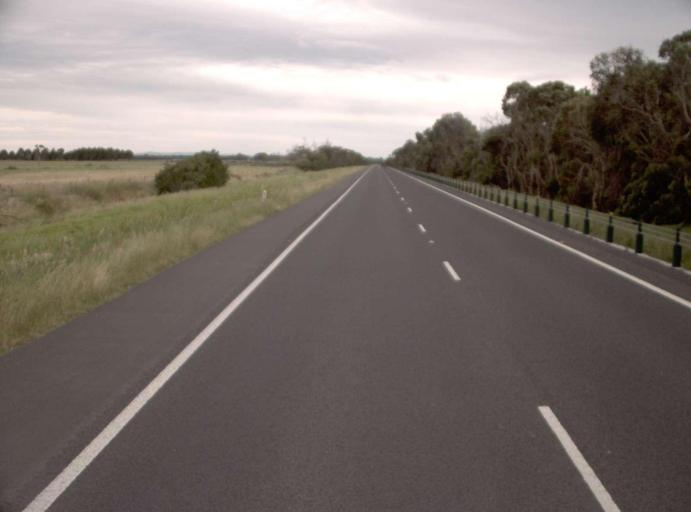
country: AU
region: Victoria
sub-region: Casey
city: Junction Village
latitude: -38.1679
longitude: 145.3269
